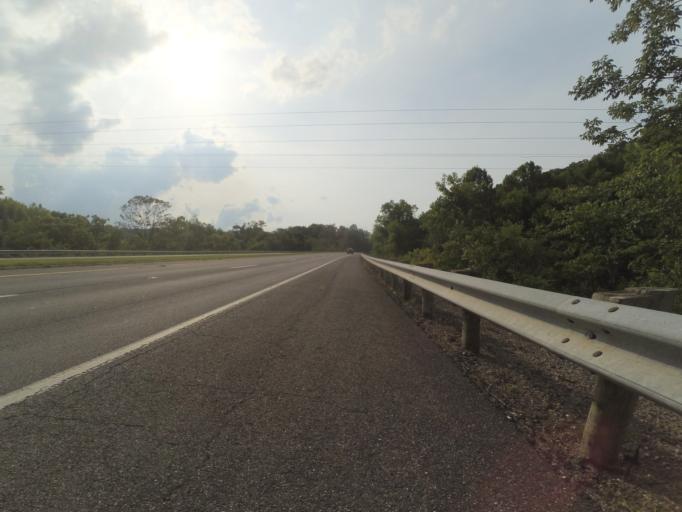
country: US
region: West Virginia
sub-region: Cabell County
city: Huntington
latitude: 38.3976
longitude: -82.4200
